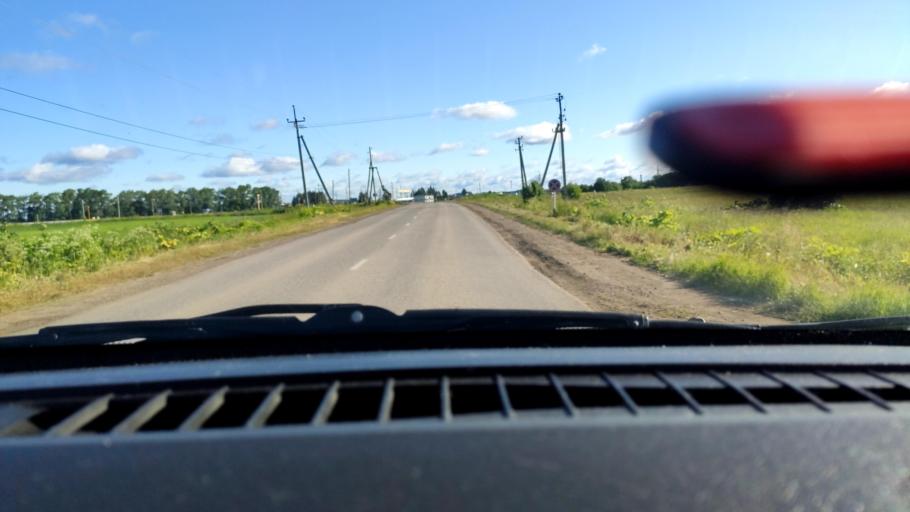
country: RU
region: Perm
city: Kultayevo
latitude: 57.8816
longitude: 55.9228
